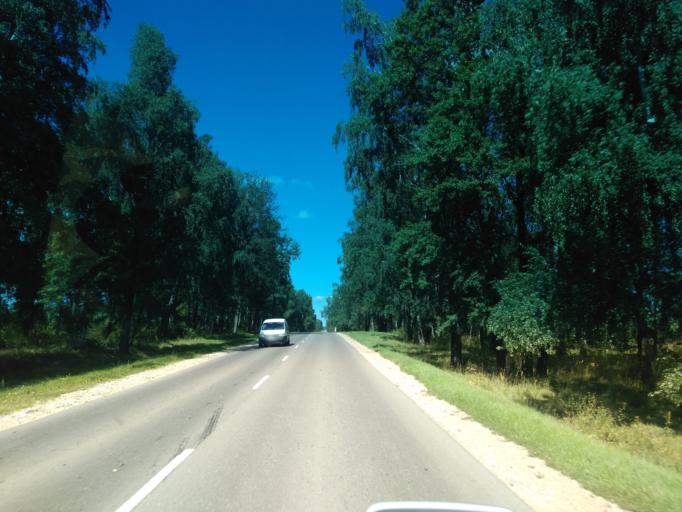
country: BY
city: Fanipol
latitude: 53.7032
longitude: 27.3518
